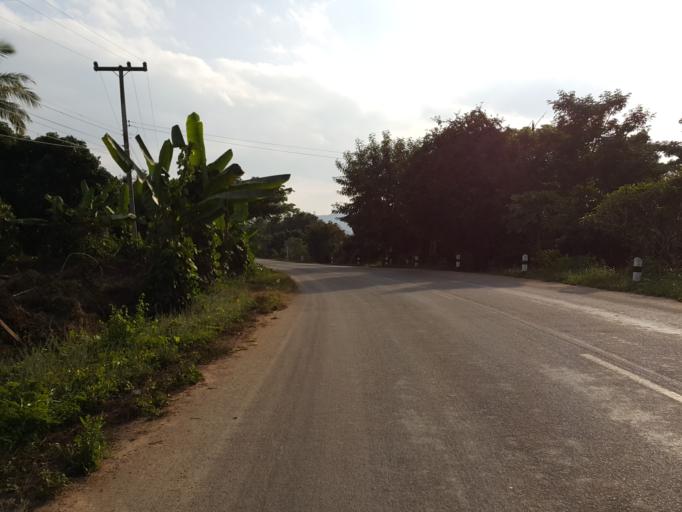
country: TH
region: Lamphun
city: Thung Hua Chang
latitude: 18.1231
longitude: 99.0149
